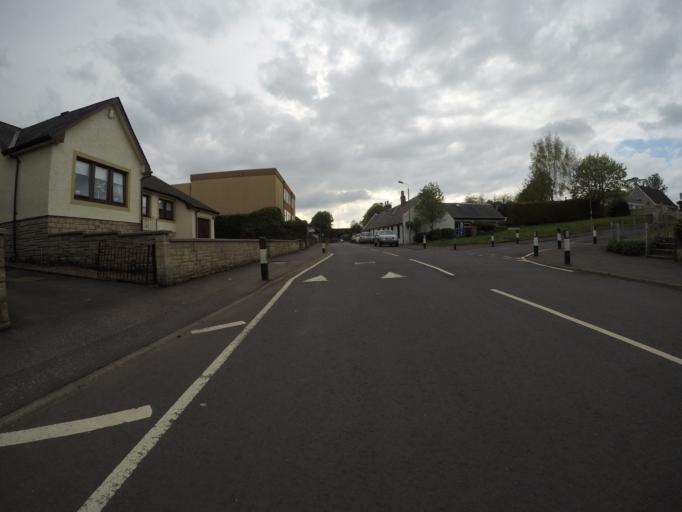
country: GB
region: Scotland
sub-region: East Ayrshire
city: Kilmaurs
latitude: 55.6386
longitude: -4.5281
